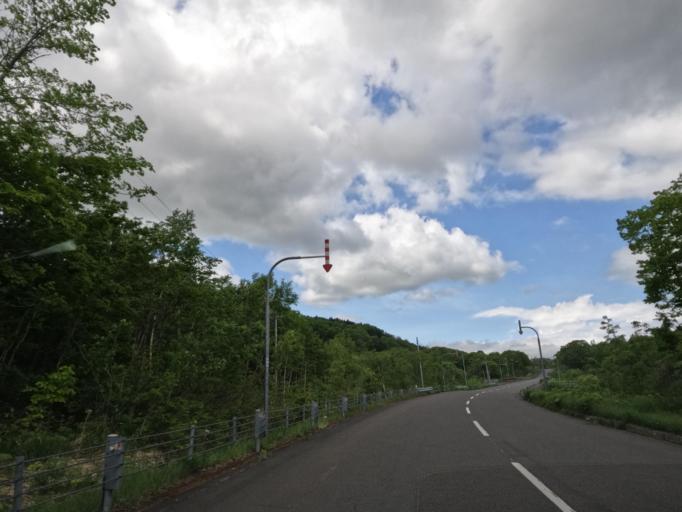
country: JP
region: Hokkaido
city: Tobetsu
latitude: 43.4670
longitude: 141.5982
